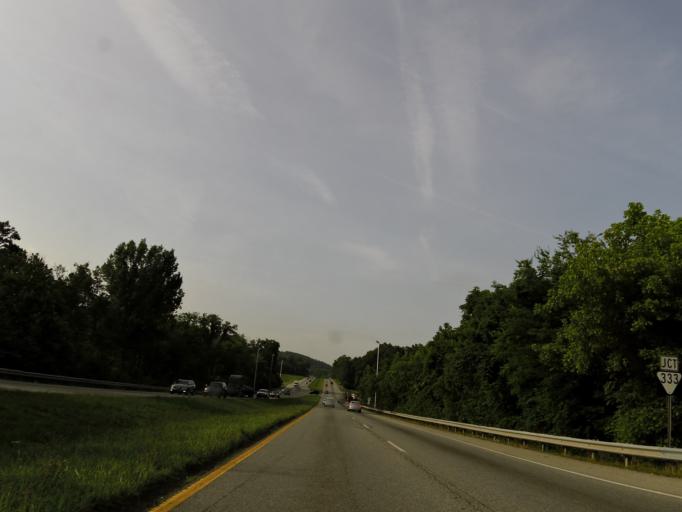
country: US
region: Tennessee
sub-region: Blount County
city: Eagleton Village
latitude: 35.8686
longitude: -83.9597
